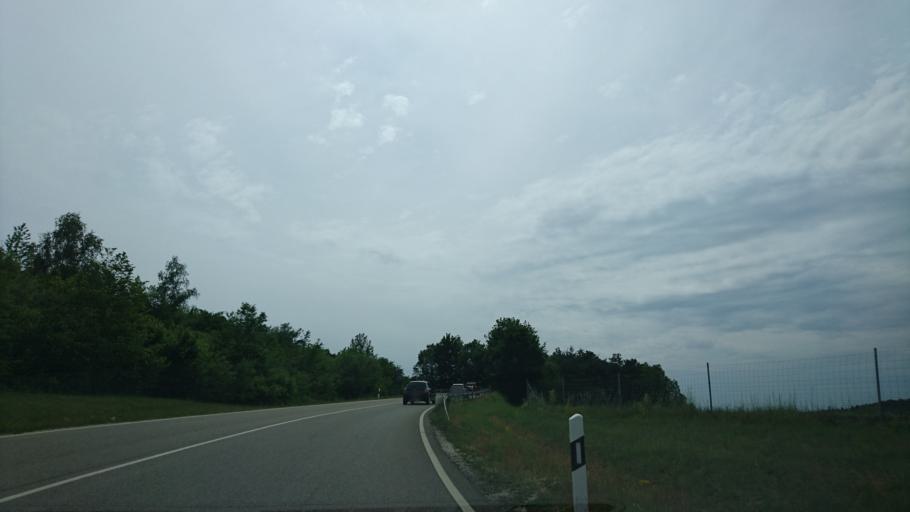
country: DE
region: Bavaria
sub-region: Regierungsbezirk Mittelfranken
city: Pleinfeld
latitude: 49.0950
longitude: 10.9860
